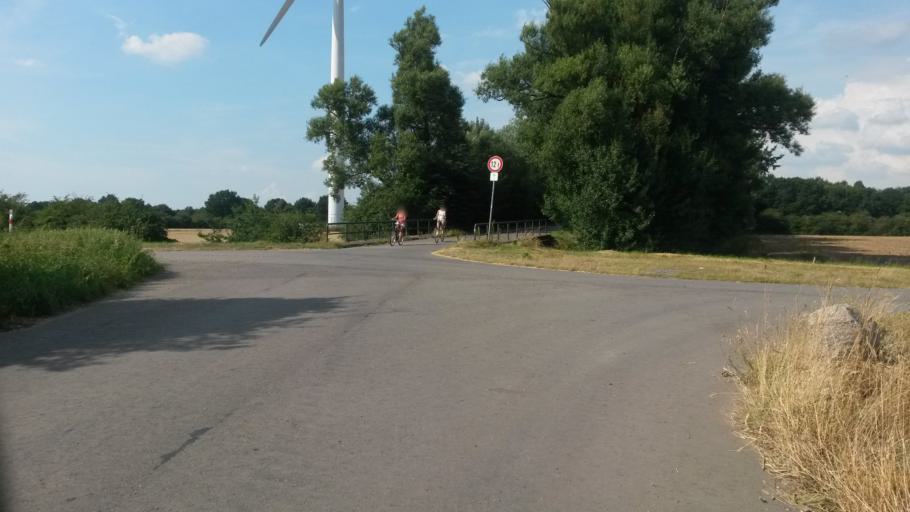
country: DE
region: Lower Saxony
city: Riede
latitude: 53.0259
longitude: 8.9312
